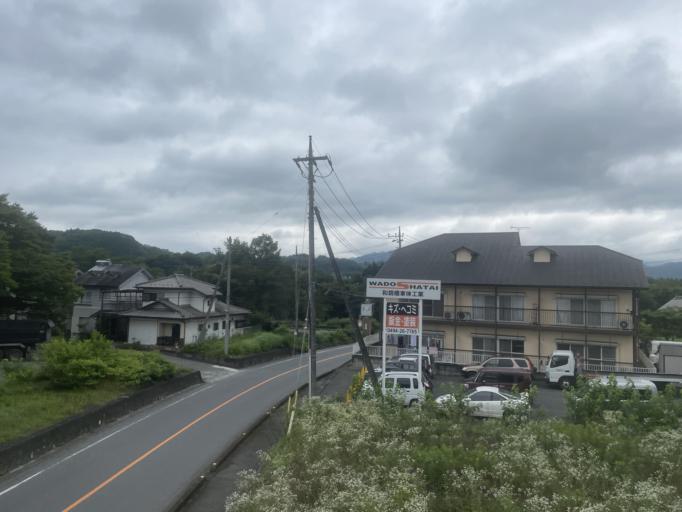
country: JP
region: Saitama
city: Chichibu
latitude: 36.0448
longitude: 139.1012
